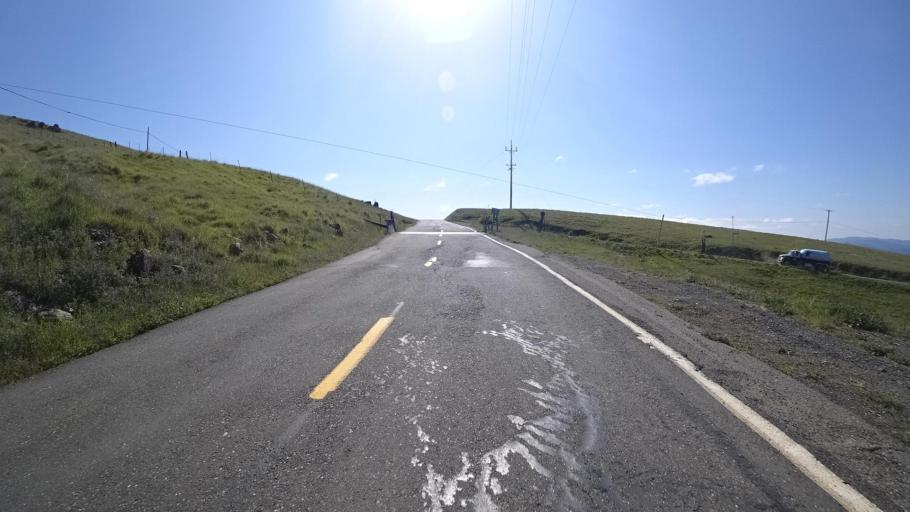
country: US
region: California
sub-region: Humboldt County
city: Redway
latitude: 40.1048
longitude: -123.7104
